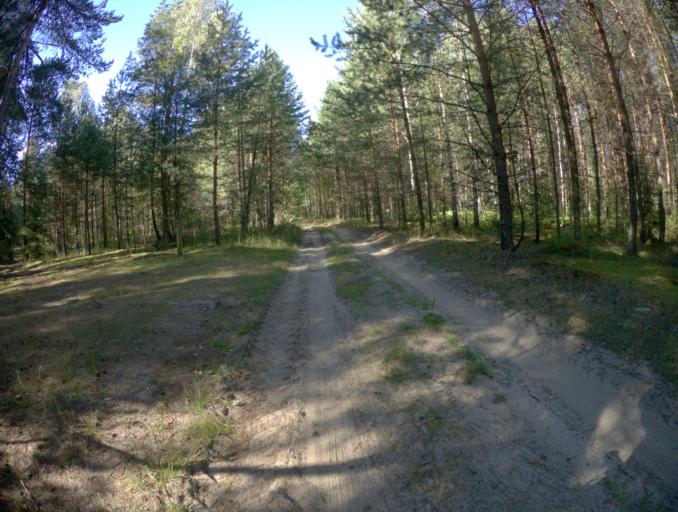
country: RU
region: Vladimir
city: Dobryatino
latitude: 55.7318
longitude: 41.4935
